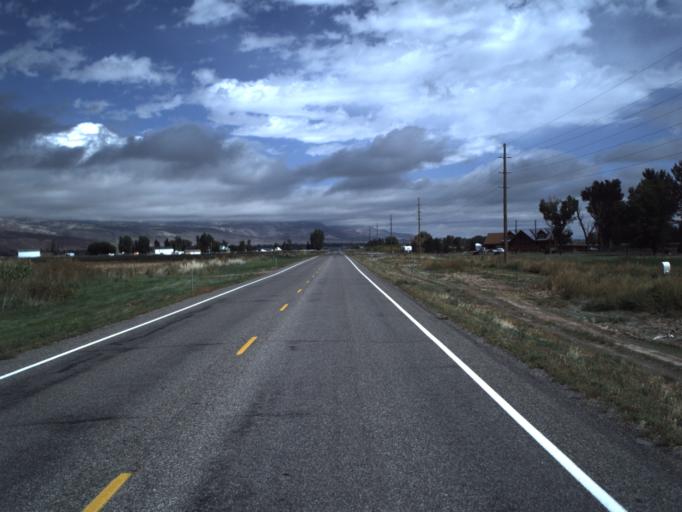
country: US
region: Utah
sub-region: Sevier County
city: Richfield
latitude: 38.7093
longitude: -112.1072
